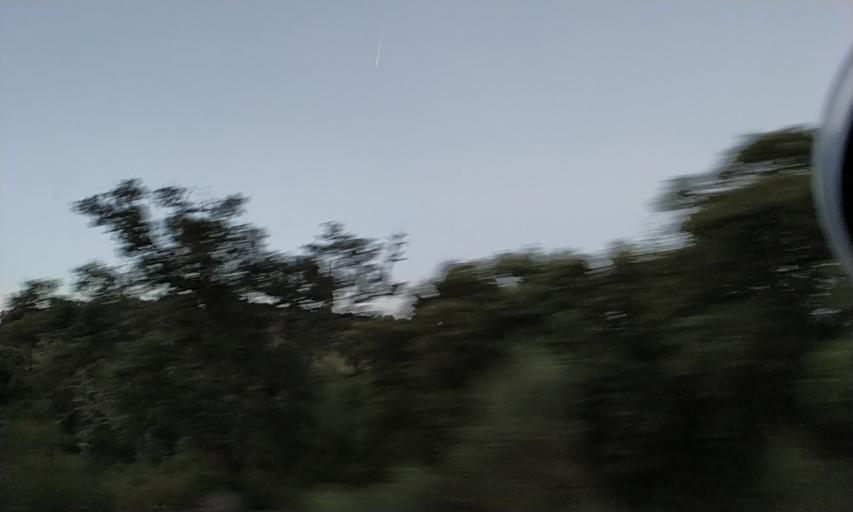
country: ES
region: Extremadura
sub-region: Provincia de Caceres
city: Alcantara
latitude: 39.7457
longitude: -6.9019
